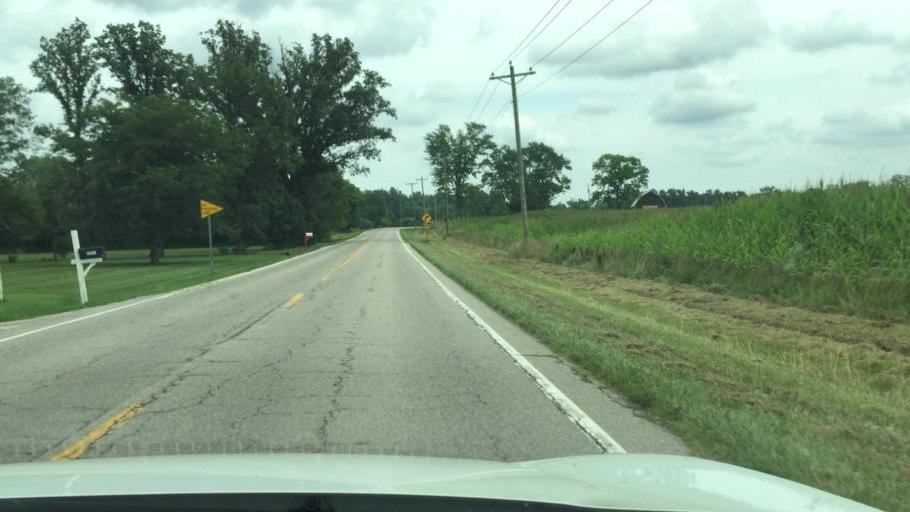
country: US
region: Ohio
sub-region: Champaign County
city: North Lewisburg
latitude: 40.2347
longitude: -83.4670
